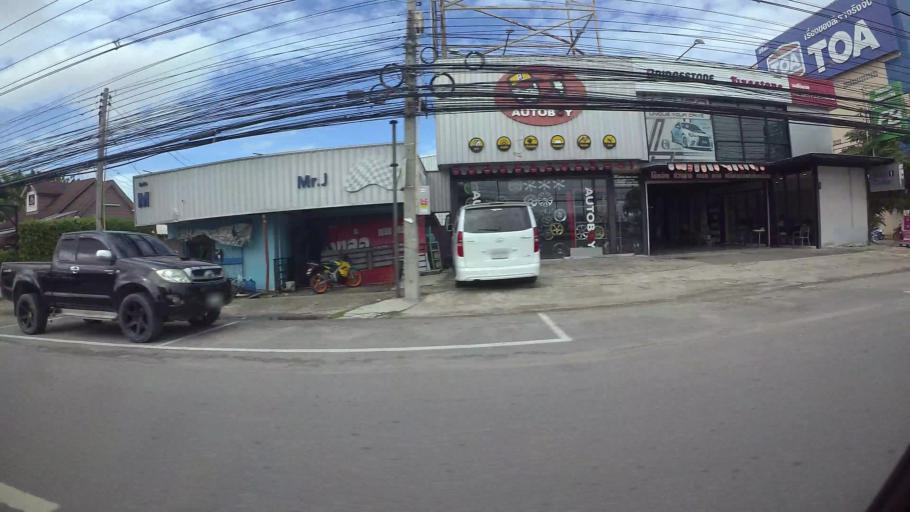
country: TH
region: Rayong
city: Rayong
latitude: 12.7153
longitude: 101.1649
